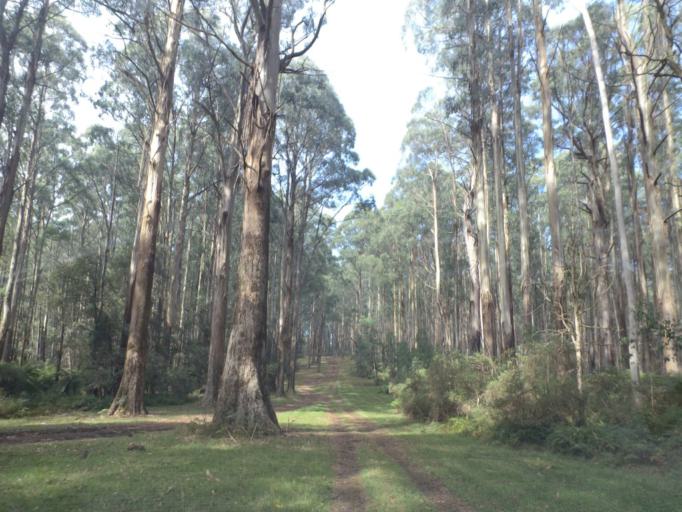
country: AU
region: Victoria
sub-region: Yarra Ranges
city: Healesville
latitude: -37.5733
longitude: 145.6020
